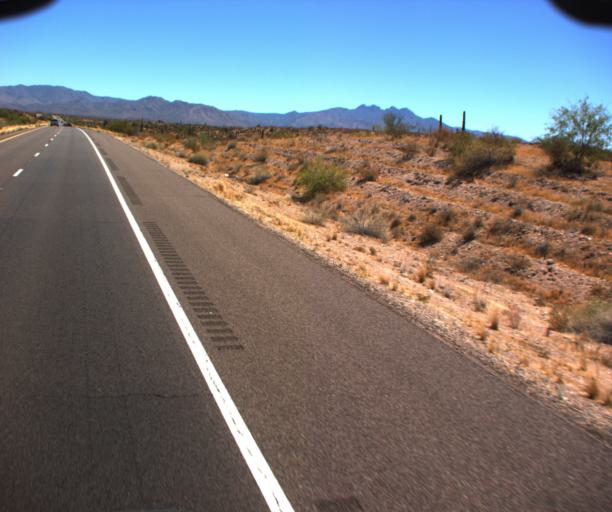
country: US
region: Arizona
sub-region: Maricopa County
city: Rio Verde
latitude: 33.6352
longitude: -111.5477
